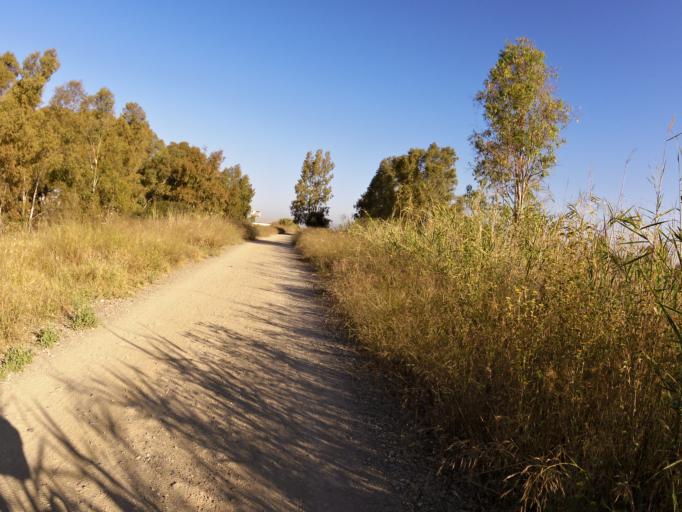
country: ES
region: Andalusia
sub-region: Provincia de Malaga
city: Torremolinos
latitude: 36.6749
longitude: -4.4698
